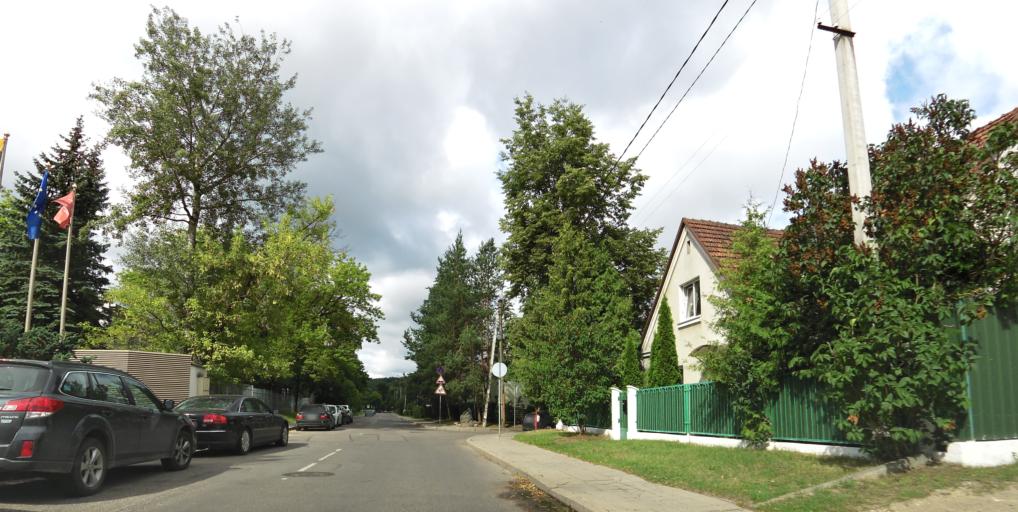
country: LT
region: Vilnius County
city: Seskine
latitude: 54.6949
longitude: 25.2476
